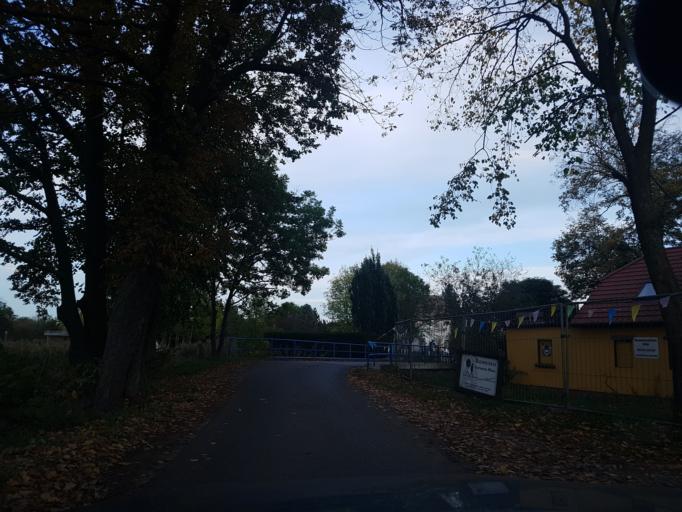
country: DE
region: Saxony
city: Nauwalde
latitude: 51.4591
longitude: 13.4547
